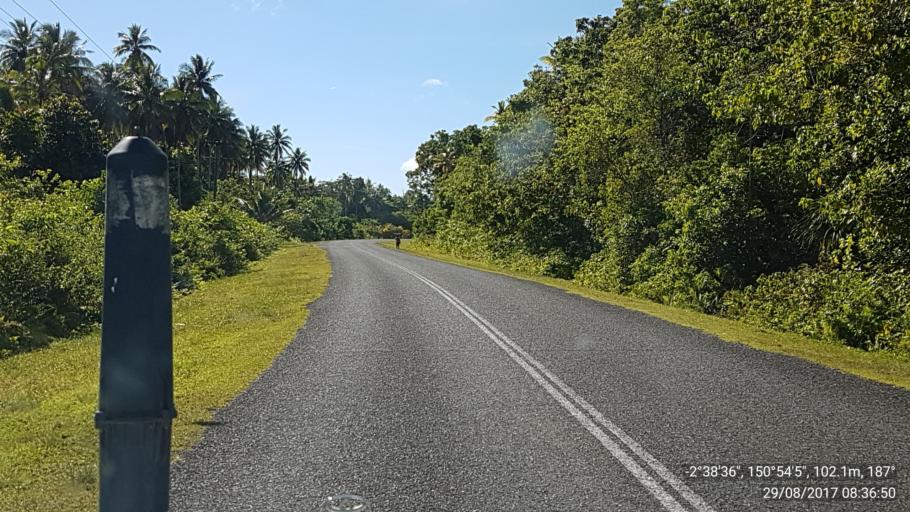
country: PG
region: New Ireland
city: Kavieng
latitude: -2.6433
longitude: 150.9017
